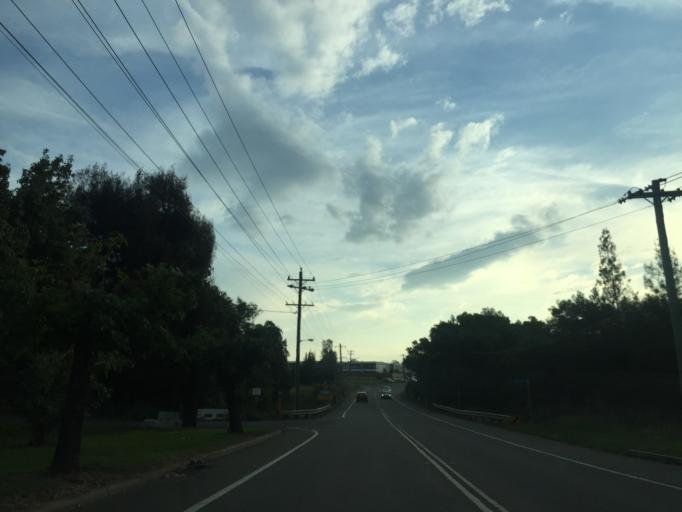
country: AU
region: New South Wales
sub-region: The Hills Shire
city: Beaumont Hills
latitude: -33.7172
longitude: 150.9564
